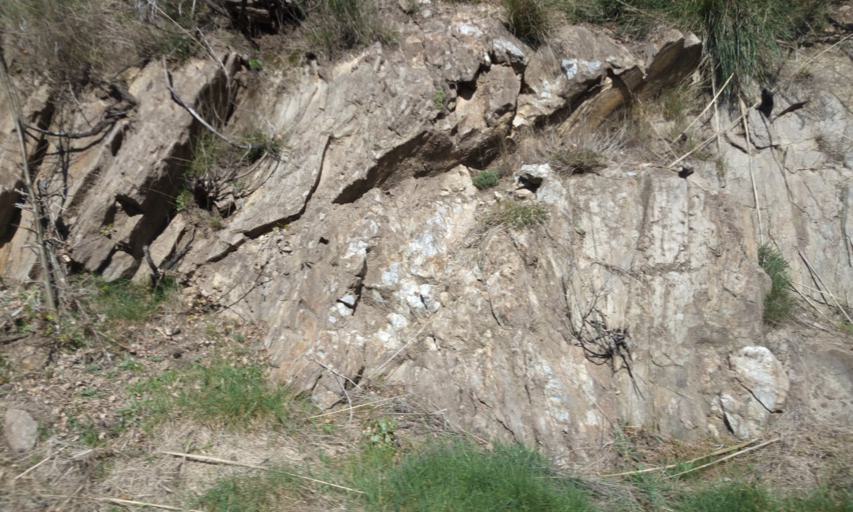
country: PT
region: Guarda
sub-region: Manteigas
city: Manteigas
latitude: 40.4868
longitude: -7.5496
